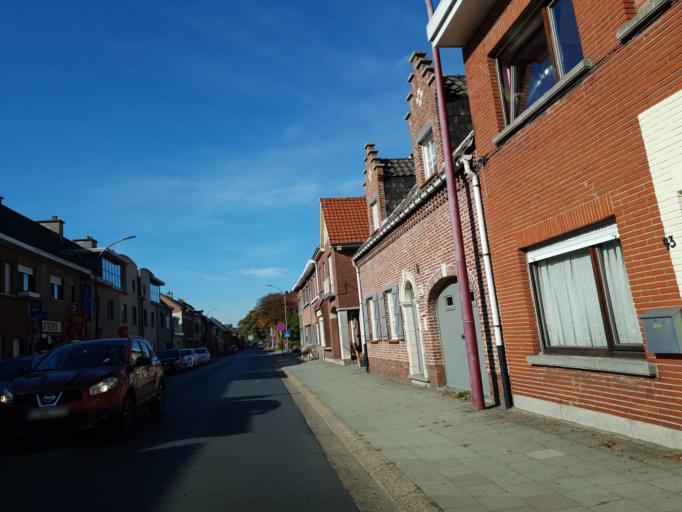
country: BE
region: Flanders
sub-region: Provincie Antwerpen
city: Stabroek
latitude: 51.3330
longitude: 4.3761
